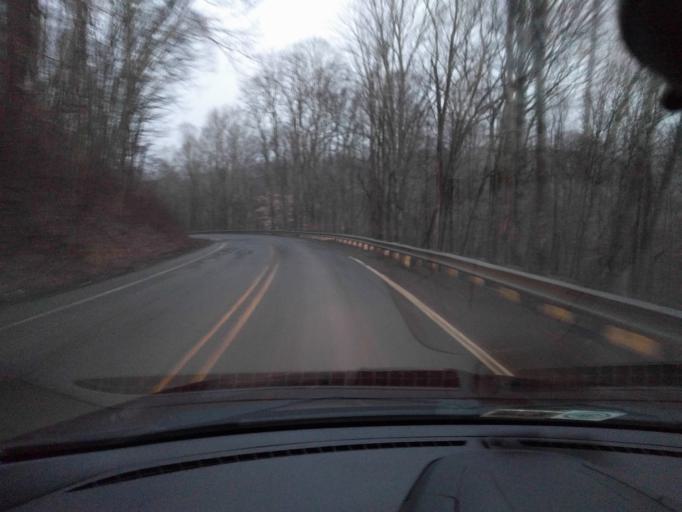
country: US
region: West Virginia
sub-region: Greenbrier County
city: Rainelle
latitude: 37.9828
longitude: -80.8339
